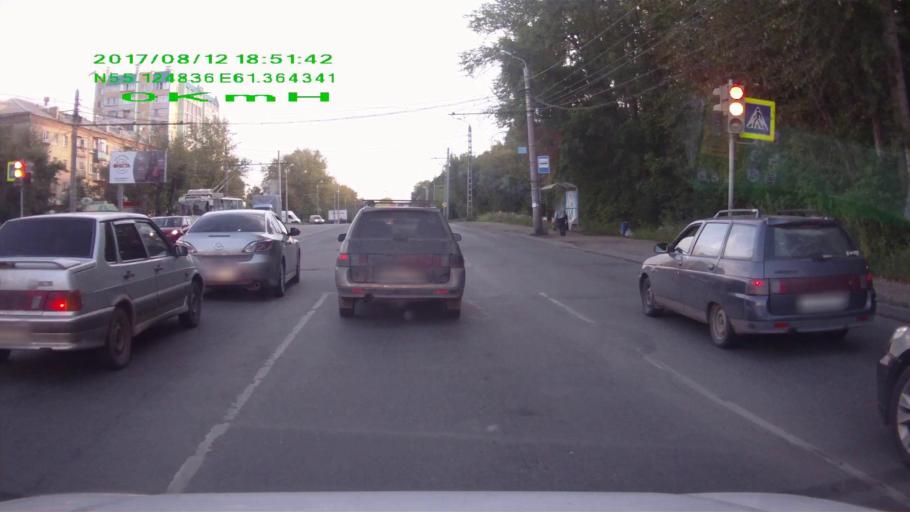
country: RU
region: Chelyabinsk
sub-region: Gorod Chelyabinsk
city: Chelyabinsk
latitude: 55.1211
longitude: 61.3627
